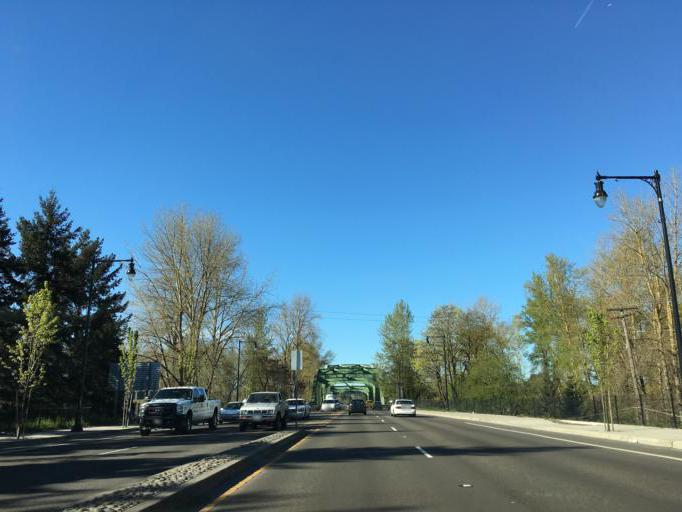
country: US
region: Oregon
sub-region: Clackamas County
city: Gladstone
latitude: 45.3711
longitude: -122.6013
